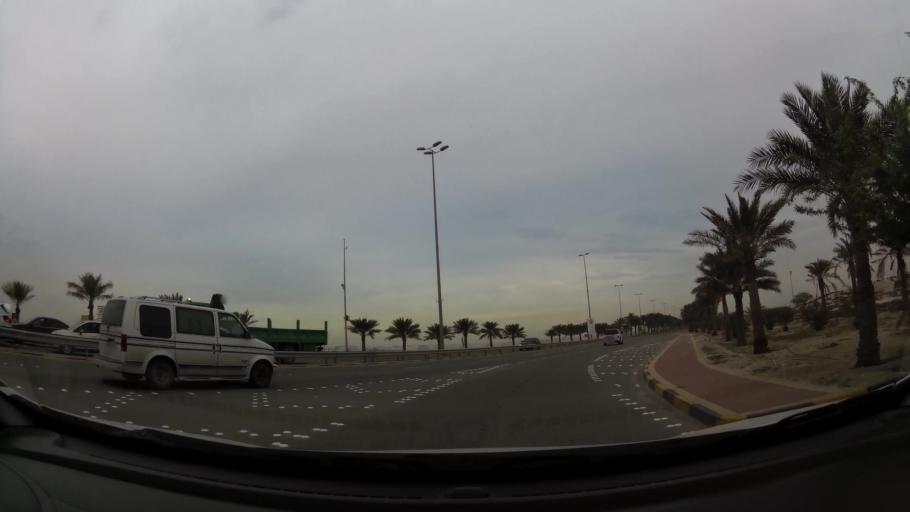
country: BH
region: Northern
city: Ar Rifa'
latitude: 26.1012
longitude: 50.5544
